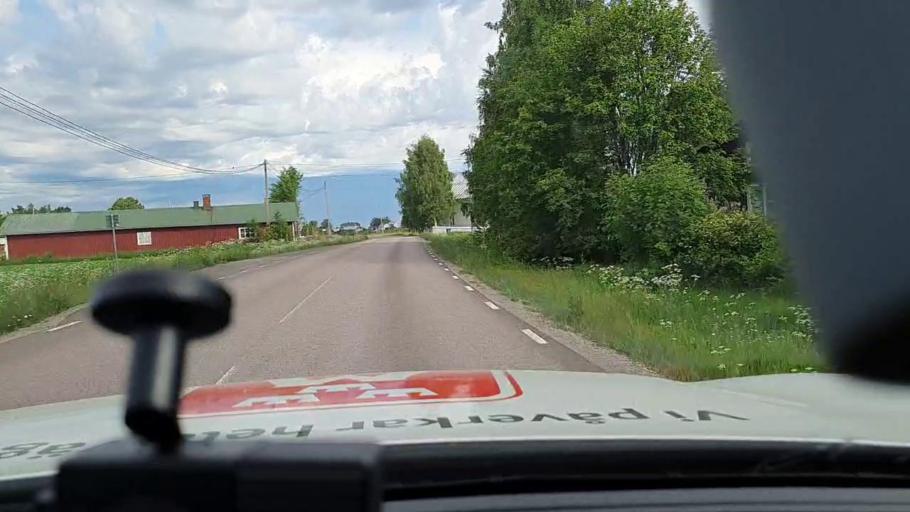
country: SE
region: Norrbotten
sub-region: Bodens Kommun
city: Saevast
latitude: 65.7029
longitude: 21.7691
